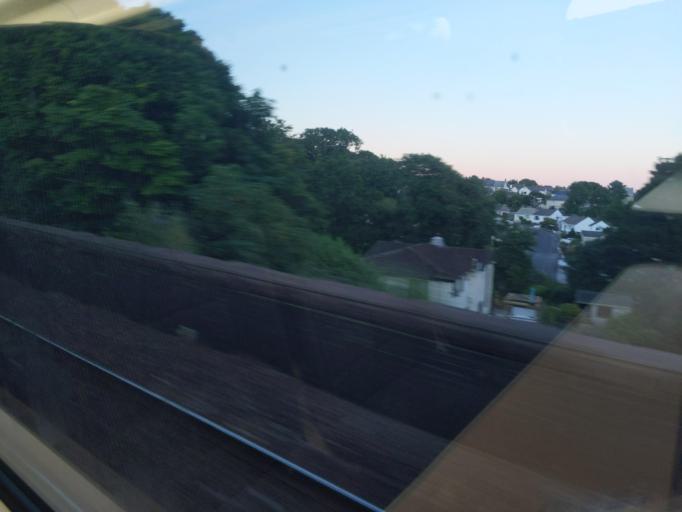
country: GB
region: England
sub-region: Cornwall
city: Truro
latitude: 50.2684
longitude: -5.0517
